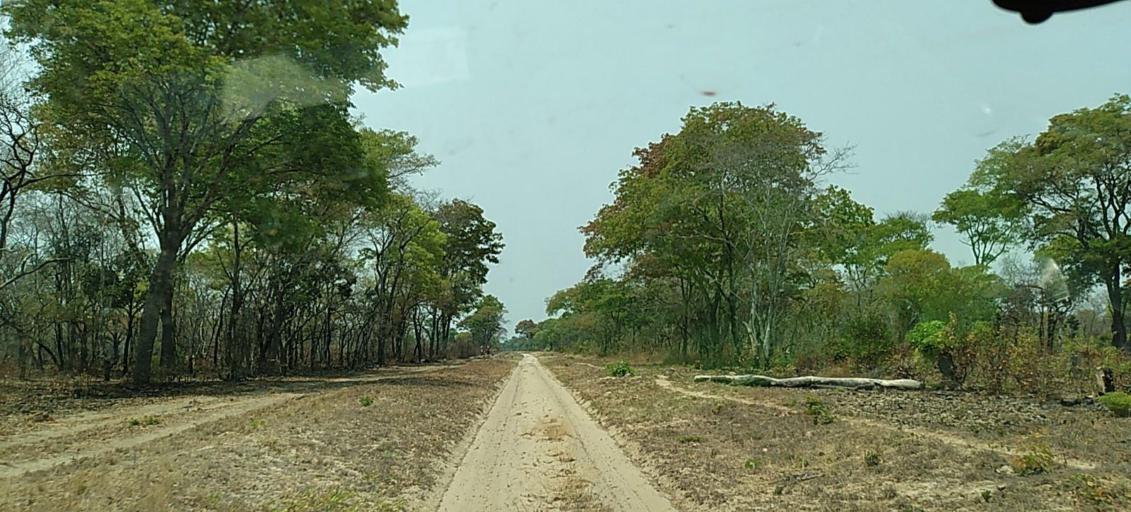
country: ZM
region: Western
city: Lukulu
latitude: -14.1428
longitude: 23.2847
